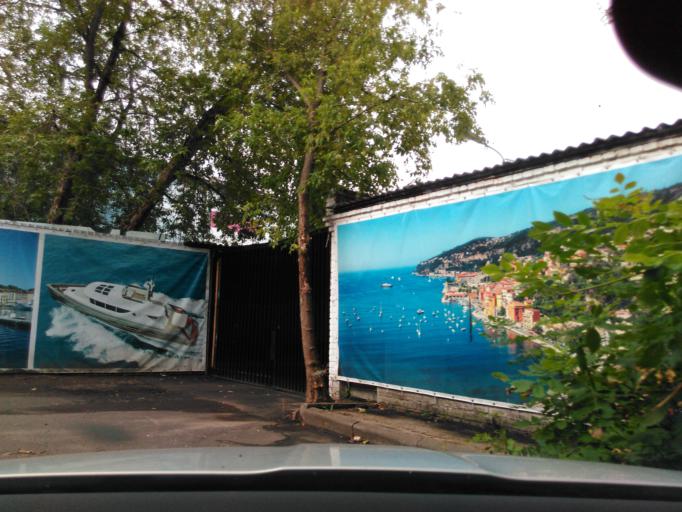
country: RU
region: Moskovskaya
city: Levoberezhnyy
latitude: 55.8285
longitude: 37.4824
